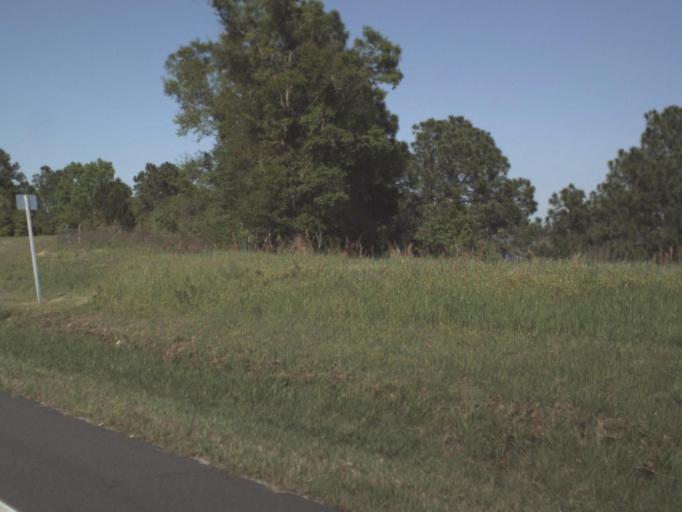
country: US
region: Florida
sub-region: Escambia County
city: East Pensacola Heights
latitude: 30.4467
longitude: -87.1730
